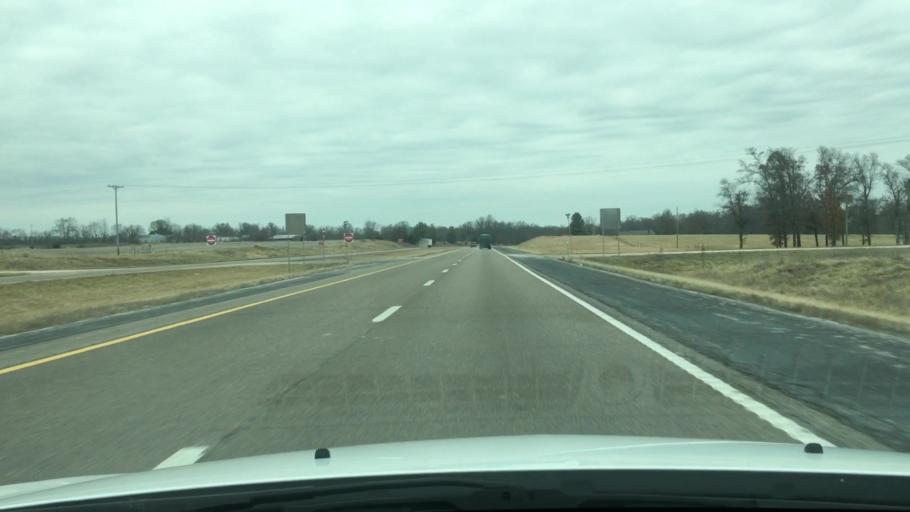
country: US
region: Missouri
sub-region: Audrain County
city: Mexico
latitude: 39.0373
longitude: -91.8906
